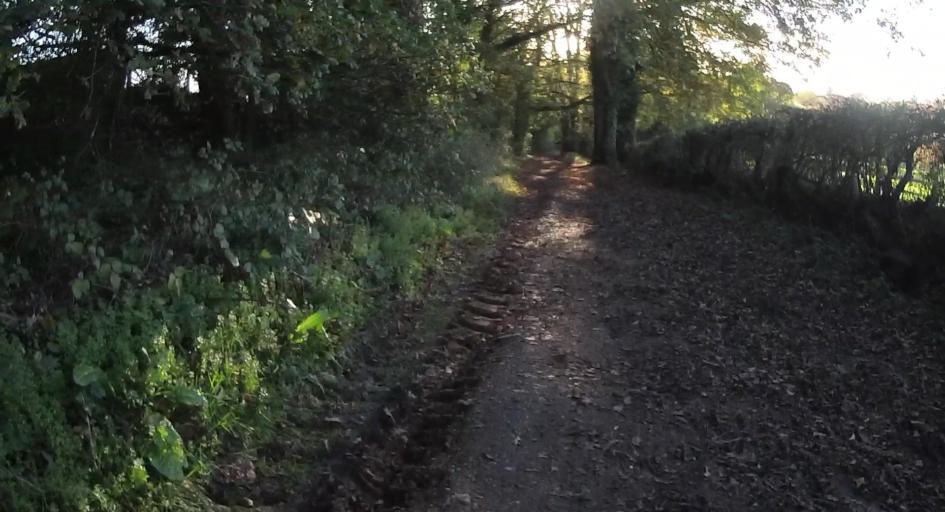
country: GB
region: England
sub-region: Wokingham
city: Barkham
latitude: 51.4017
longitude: -0.8971
